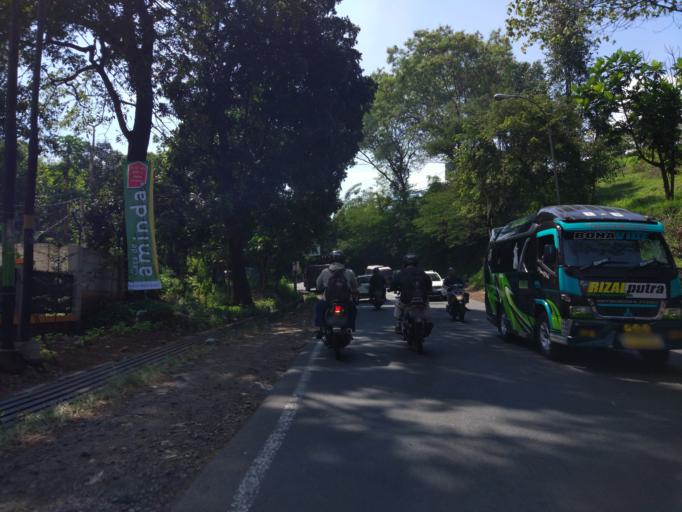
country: ID
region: West Java
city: Cileunyi
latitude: -6.9270
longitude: 107.7849
